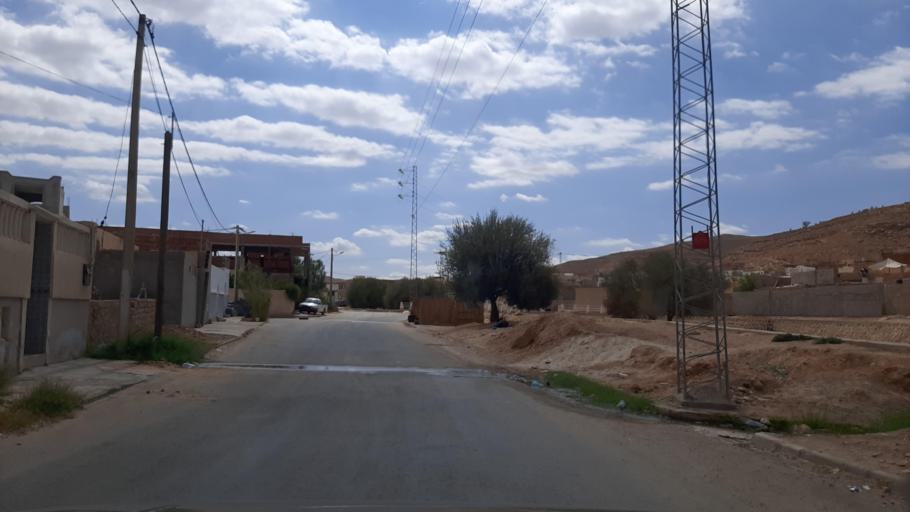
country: TN
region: Tataouine
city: Tataouine
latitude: 32.9275
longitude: 10.4581
